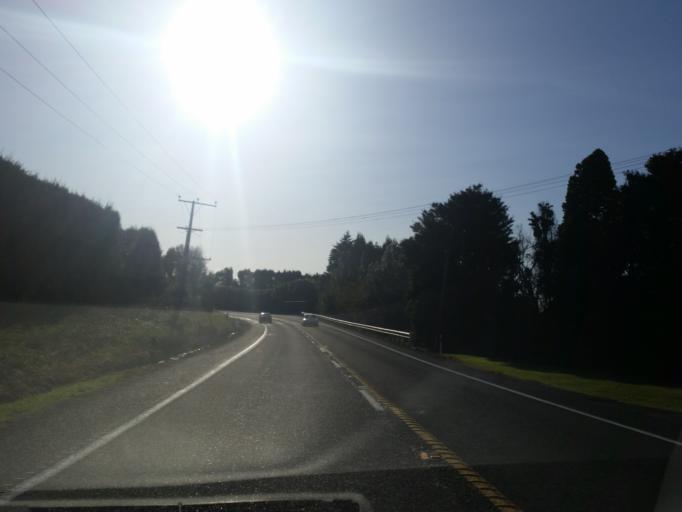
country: NZ
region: Bay of Plenty
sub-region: Western Bay of Plenty District
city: Katikati
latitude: -37.5245
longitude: 175.9184
